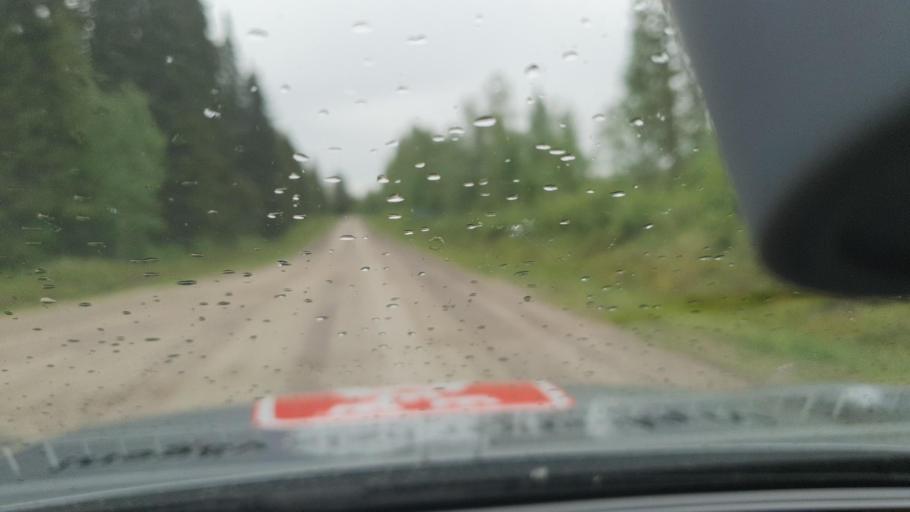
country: SE
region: Norrbotten
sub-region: Kalix Kommun
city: Rolfs
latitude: 66.0771
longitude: 22.9681
